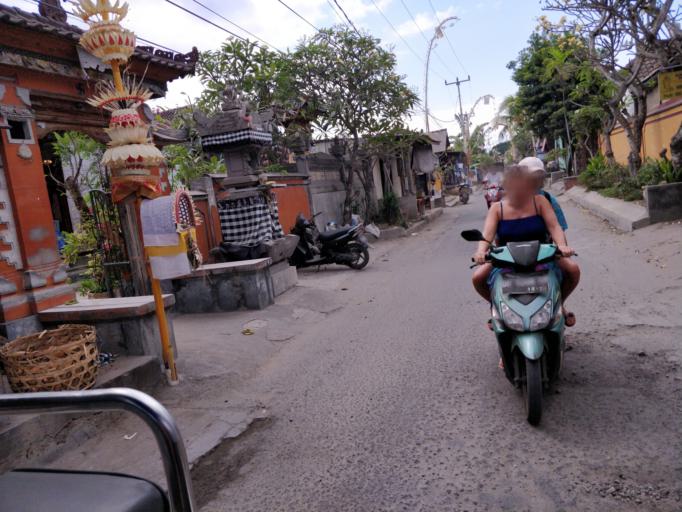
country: ID
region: Bali
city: Jungutbatu Kaja Dua
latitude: -8.6777
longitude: 115.4475
